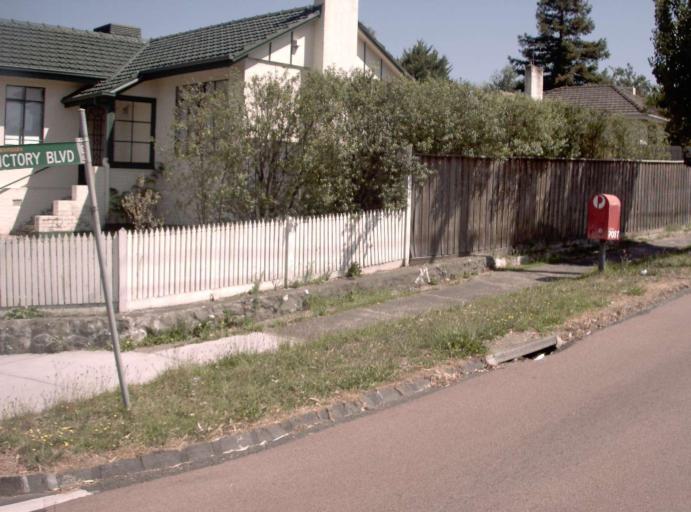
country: AU
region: Victoria
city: Ashburton
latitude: -37.8706
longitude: 145.0920
